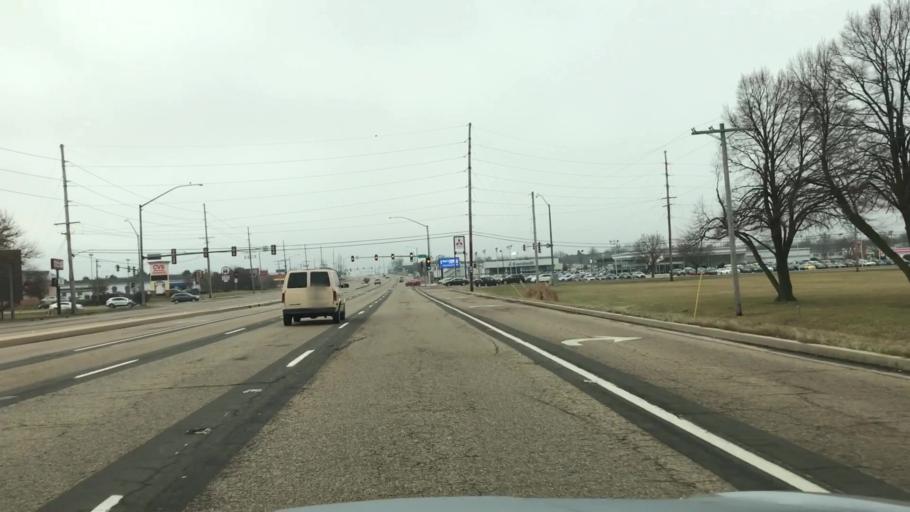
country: US
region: Illinois
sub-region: McLean County
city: Normal
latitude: 40.5191
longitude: -88.9529
